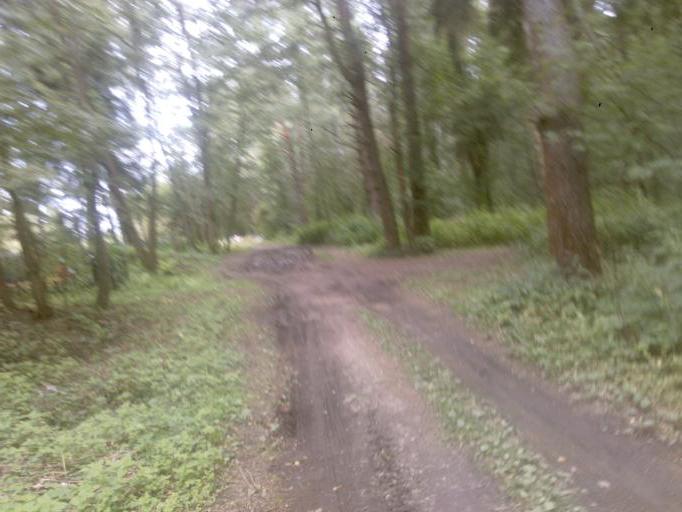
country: RU
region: Moskovskaya
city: Solnechnogorsk
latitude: 56.1383
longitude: 36.9292
